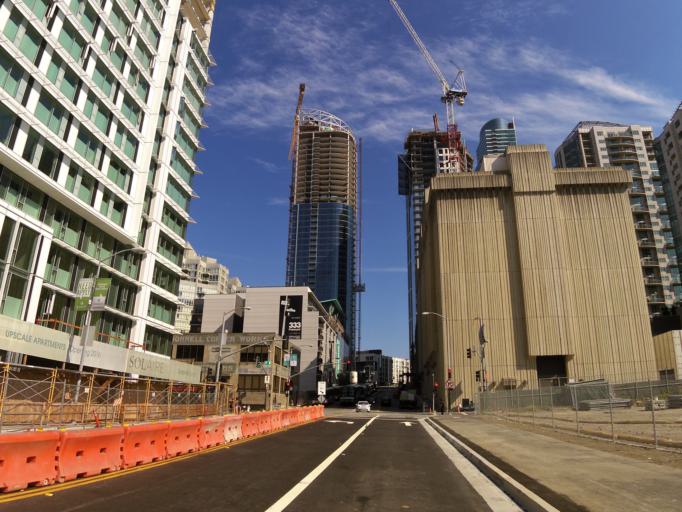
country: US
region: California
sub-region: San Francisco County
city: San Francisco
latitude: 37.7884
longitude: -122.3942
